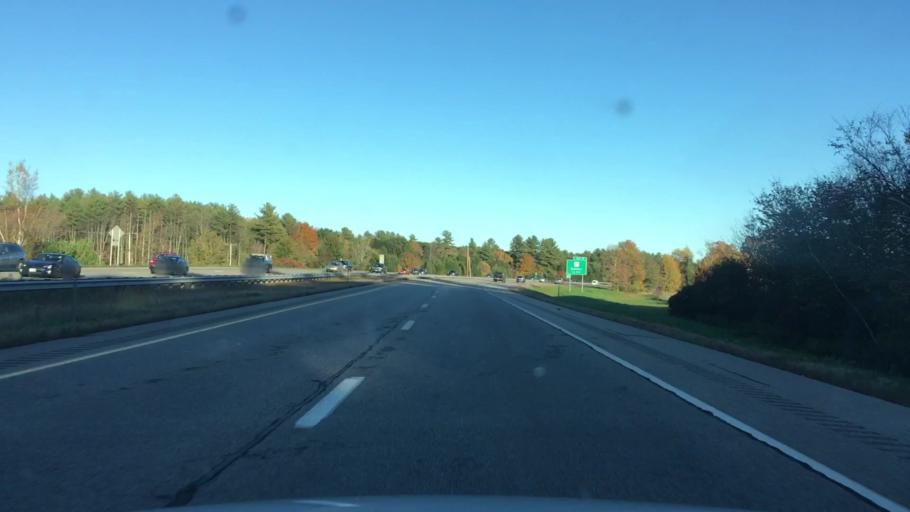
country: US
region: New Hampshire
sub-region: Rockingham County
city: Exeter
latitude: 43.0072
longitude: -70.9933
